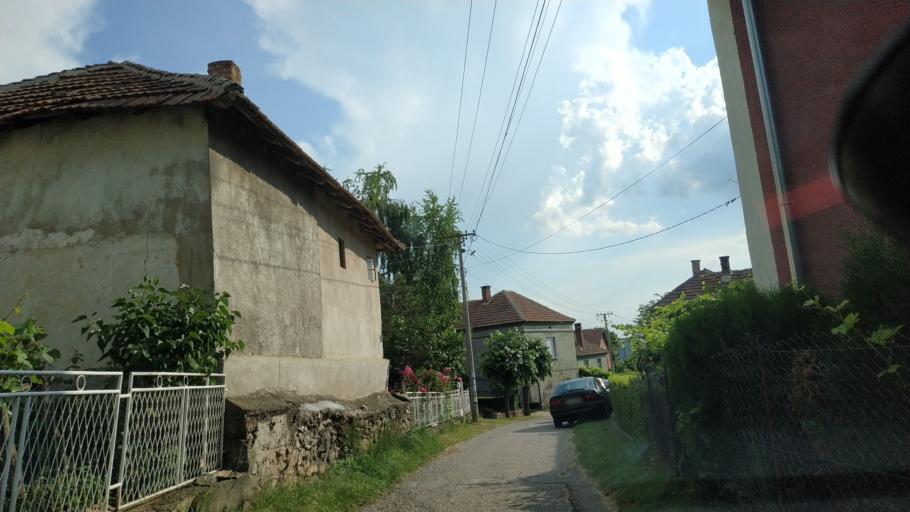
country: RS
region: Central Serbia
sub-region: Nisavski Okrug
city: Aleksinac
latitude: 43.6050
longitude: 21.6950
